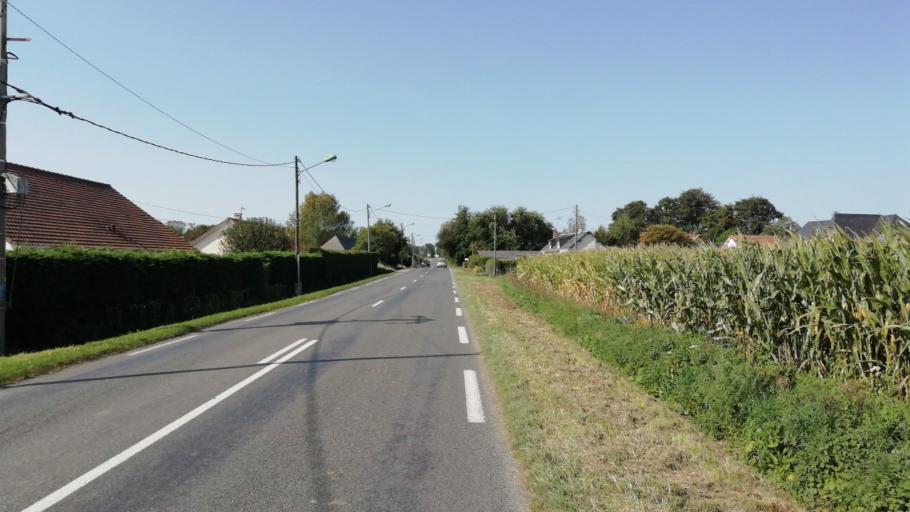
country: FR
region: Haute-Normandie
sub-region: Departement de la Seine-Maritime
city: La Remuee
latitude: 49.5264
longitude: 0.3894
